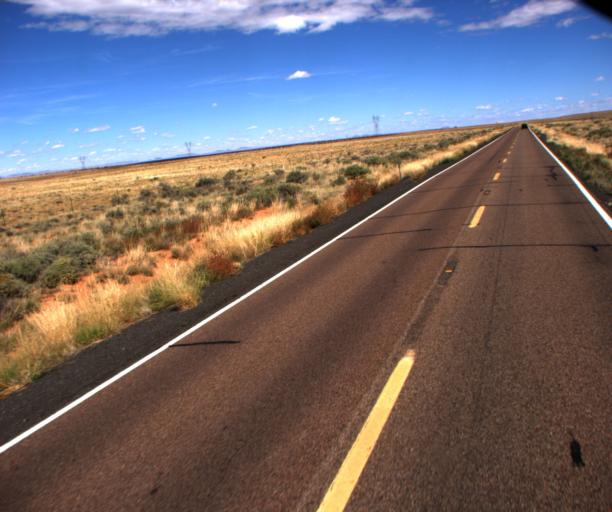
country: US
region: Arizona
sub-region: Navajo County
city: Holbrook
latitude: 34.7877
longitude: -110.2238
